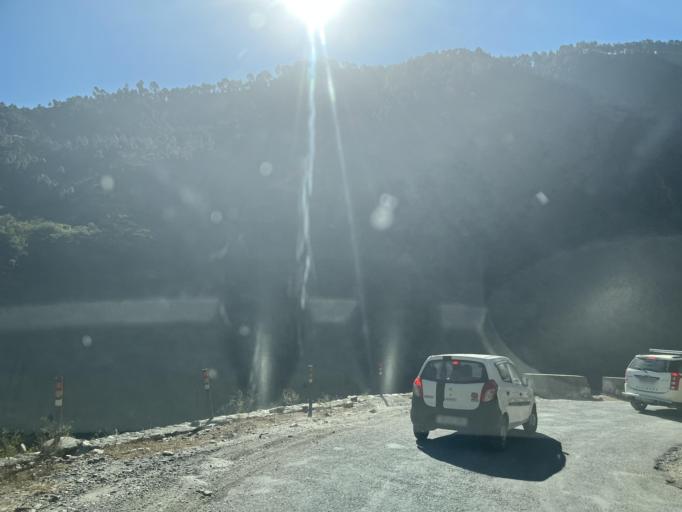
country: IN
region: Uttarakhand
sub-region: Naini Tal
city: Naini Tal
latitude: 29.5093
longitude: 79.4655
